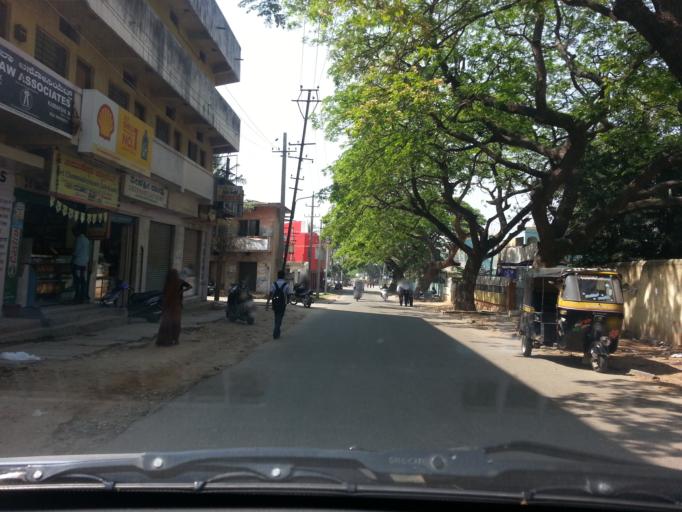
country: IN
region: Karnataka
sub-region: Mysore
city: Mysore
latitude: 12.3307
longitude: 76.6619
